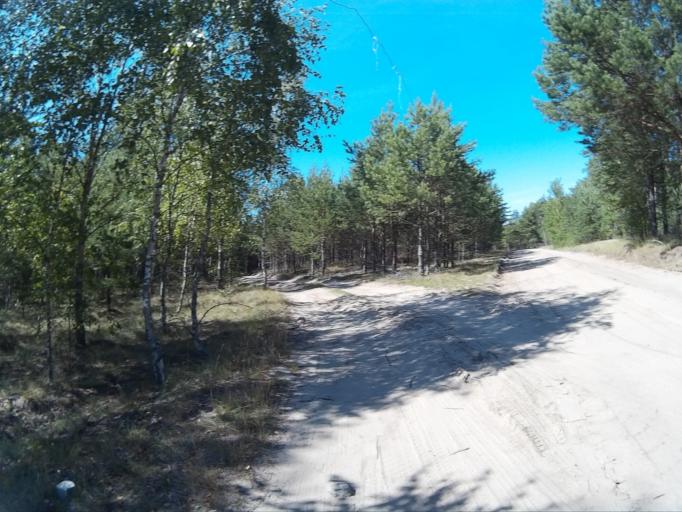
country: PL
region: Pomeranian Voivodeship
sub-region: Powiat chojnicki
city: Czersk
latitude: 53.7230
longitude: 17.9022
